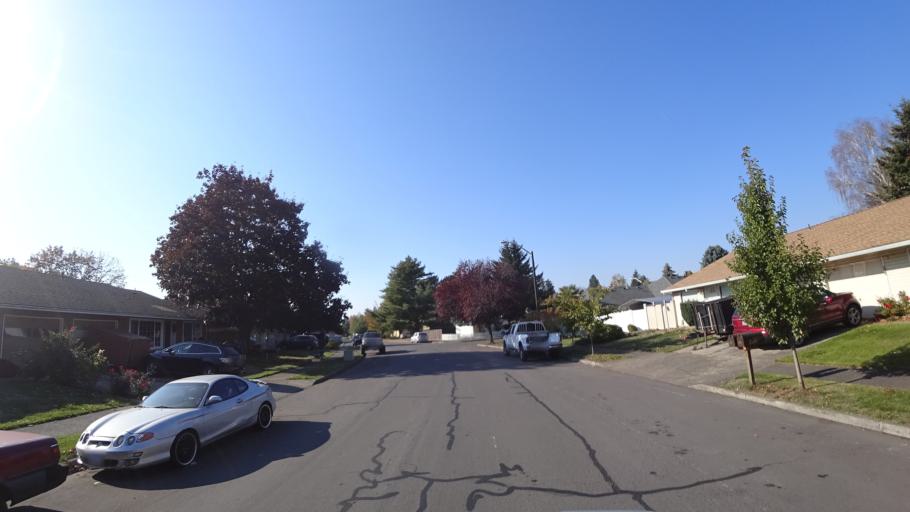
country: US
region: Oregon
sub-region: Multnomah County
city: Gresham
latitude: 45.5096
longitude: -122.4258
